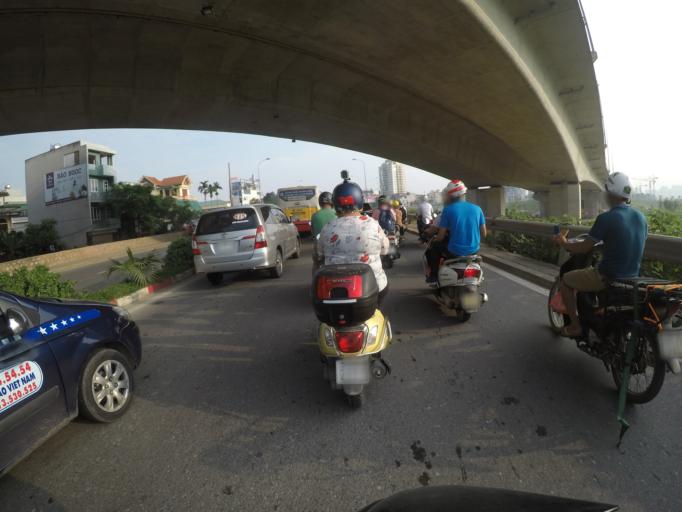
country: VN
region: Ha Noi
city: Tay Ho
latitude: 21.0847
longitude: 105.8165
